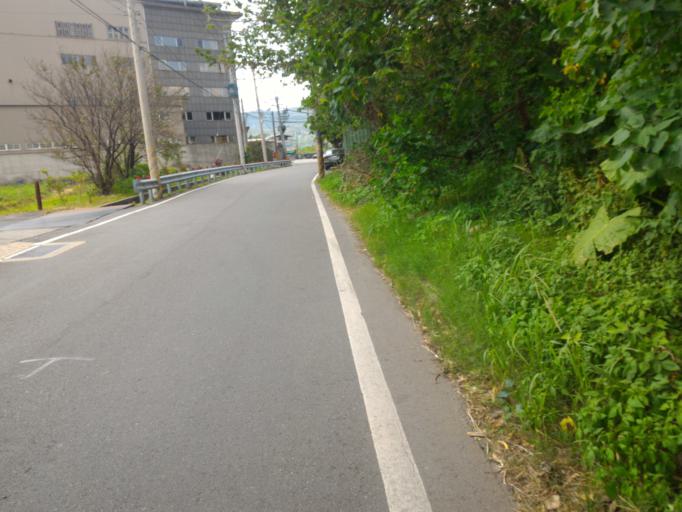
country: TW
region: Taiwan
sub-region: Taoyuan
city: Taoyuan
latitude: 24.9626
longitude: 121.3936
